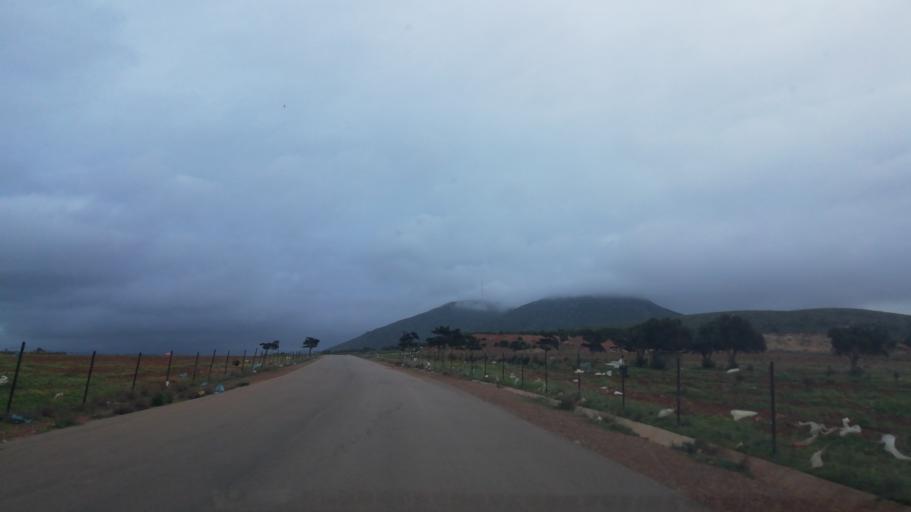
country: DZ
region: Oran
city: Bir el Djir
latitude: 35.7609
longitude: -0.5262
